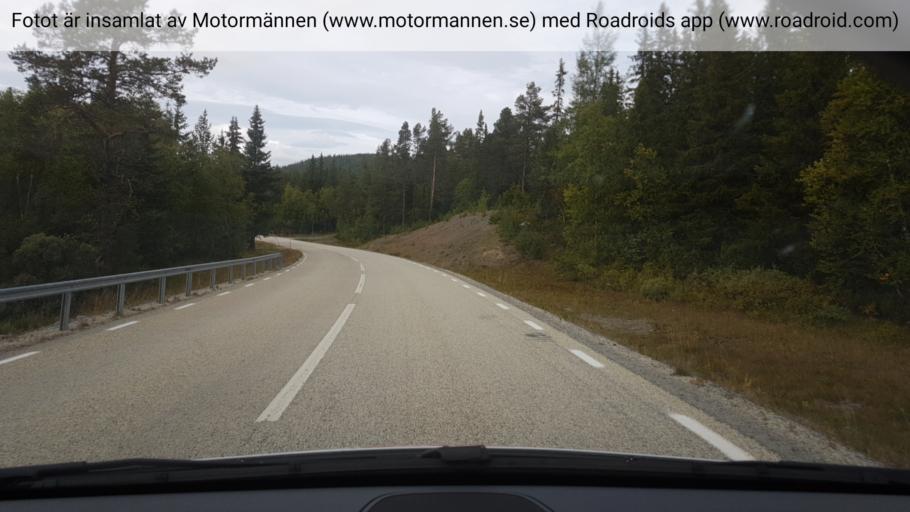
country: SE
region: Jaemtland
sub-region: Are Kommun
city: Are
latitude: 62.8471
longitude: 12.8198
